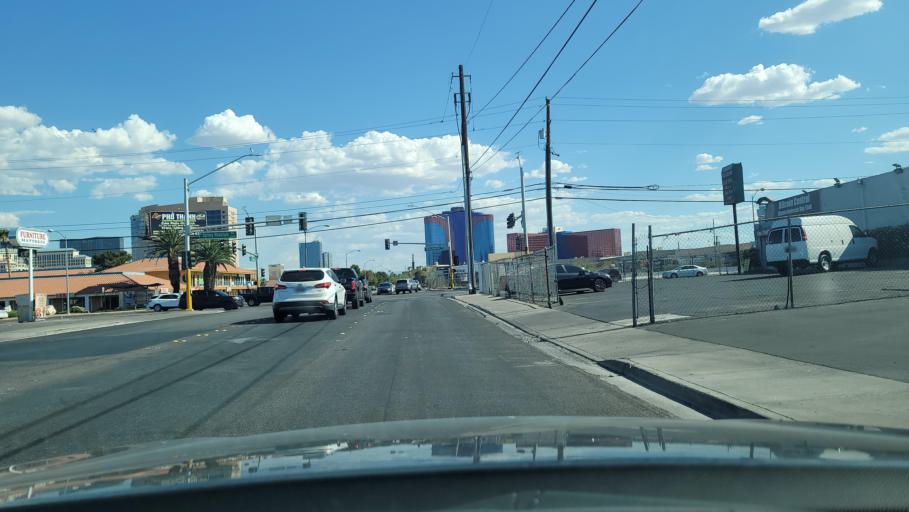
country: US
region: Nevada
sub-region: Clark County
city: Paradise
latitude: 36.1270
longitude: -115.1856
